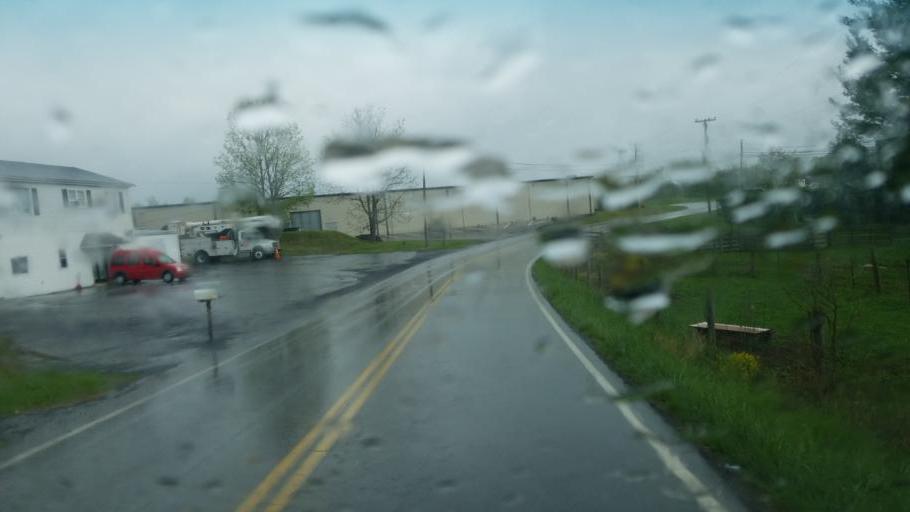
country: US
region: Virginia
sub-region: Smyth County
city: Adwolf
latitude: 36.8072
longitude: -81.5763
